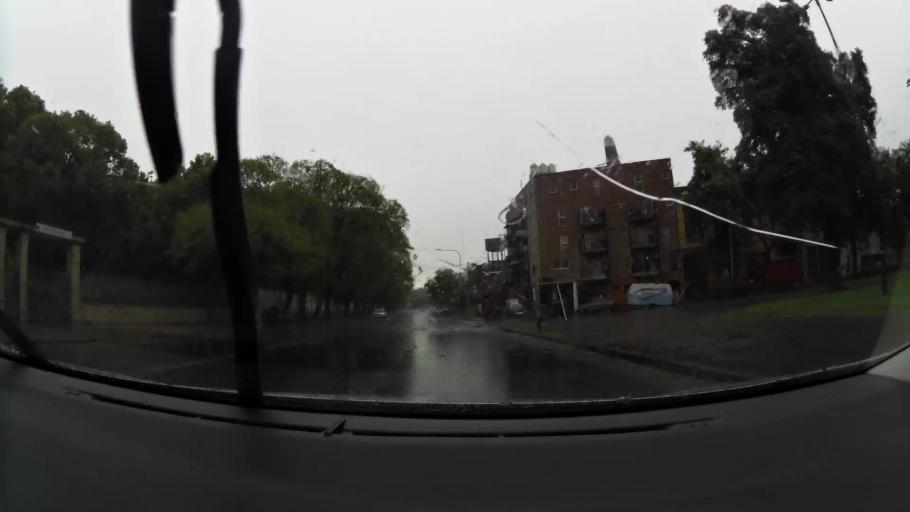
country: AR
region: Buenos Aires F.D.
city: Buenos Aires
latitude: -34.6356
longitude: -58.3854
